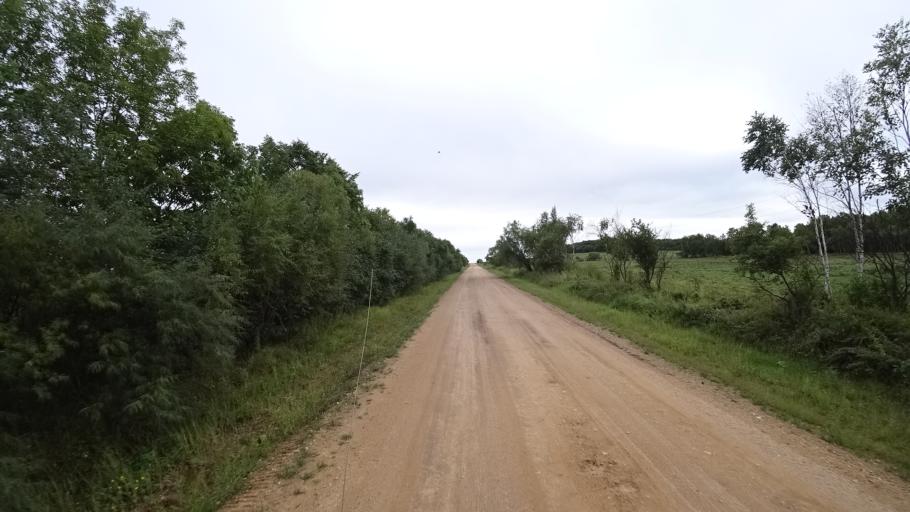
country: RU
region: Primorskiy
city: Monastyrishche
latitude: 44.0969
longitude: 132.6014
